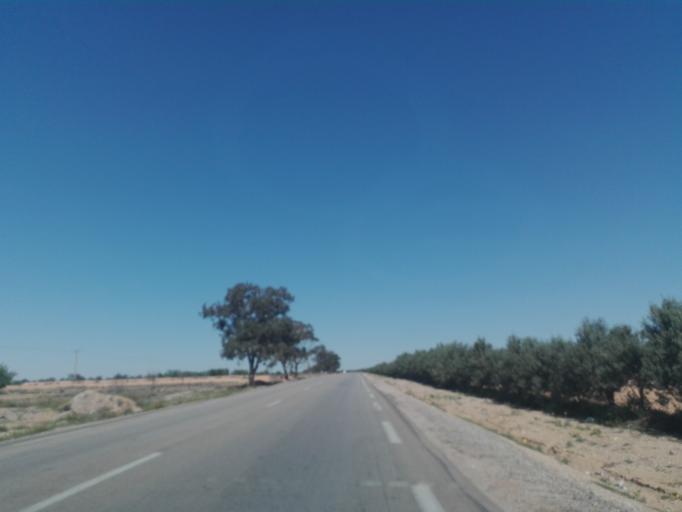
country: TN
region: Safaqis
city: Bi'r `Ali Bin Khalifah
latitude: 34.7488
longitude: 10.3512
